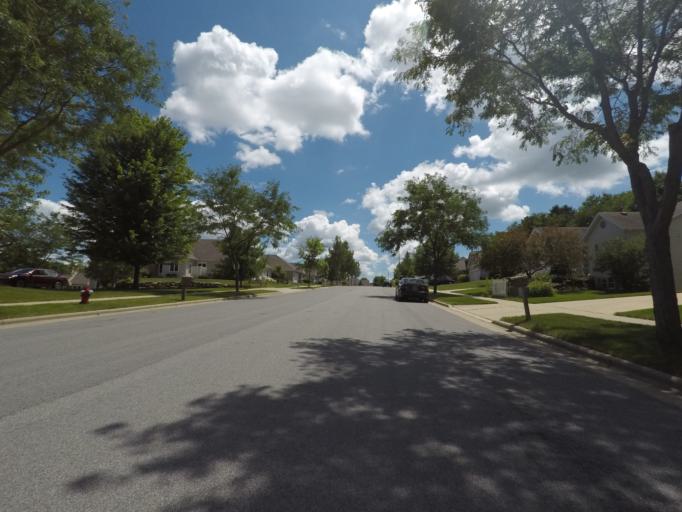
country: US
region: Wisconsin
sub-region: Dane County
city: Middleton
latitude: 43.0735
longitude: -89.5316
